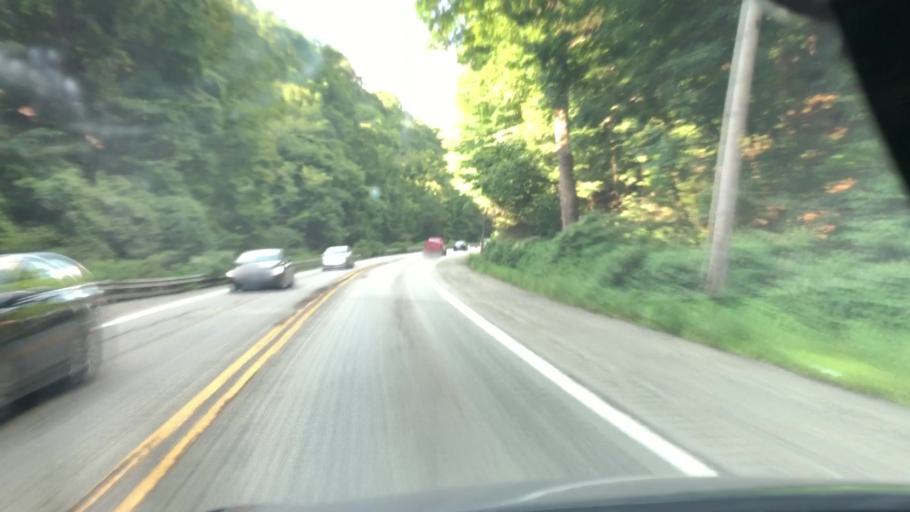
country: US
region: Pennsylvania
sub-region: Allegheny County
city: Pitcairn
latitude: 40.4105
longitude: -79.7606
